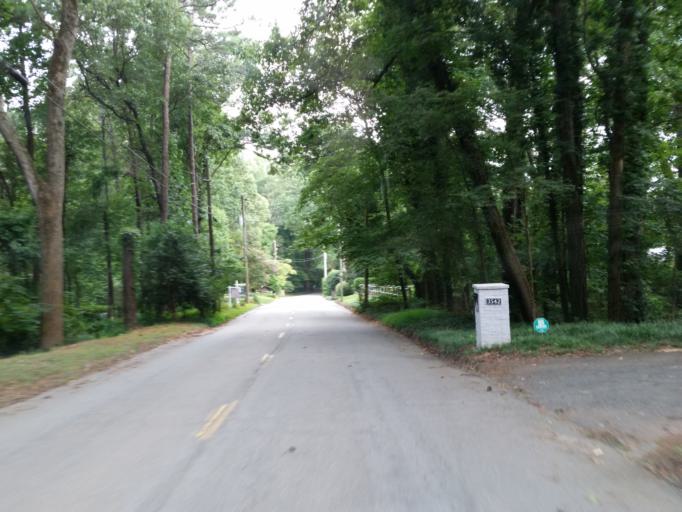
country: US
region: Georgia
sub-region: Cobb County
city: Vinings
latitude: 33.8522
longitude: -84.4415
